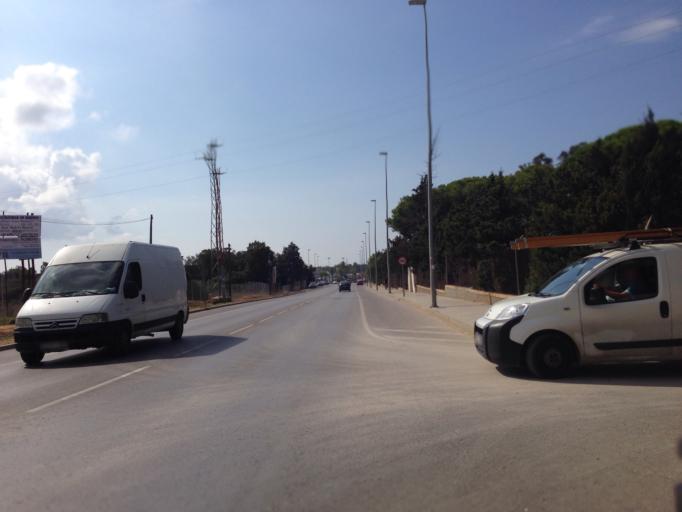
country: ES
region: Andalusia
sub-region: Provincia de Cadiz
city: Chiclana de la Frontera
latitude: 36.4032
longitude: -6.1671
